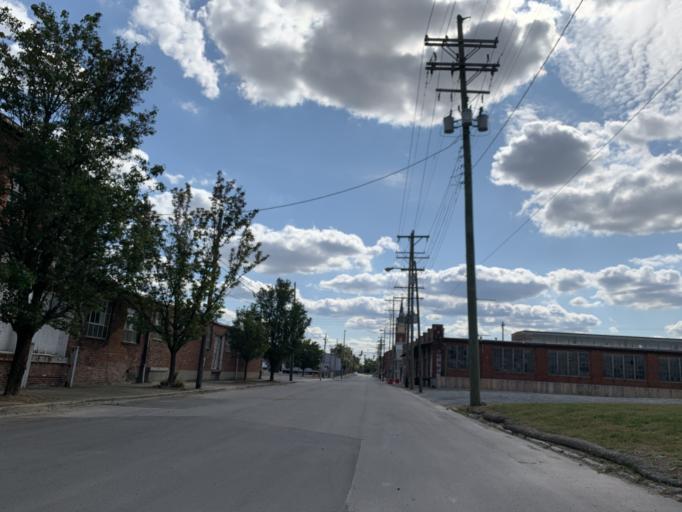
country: US
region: Kentucky
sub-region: Jefferson County
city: Louisville
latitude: 38.2595
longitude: -85.7712
